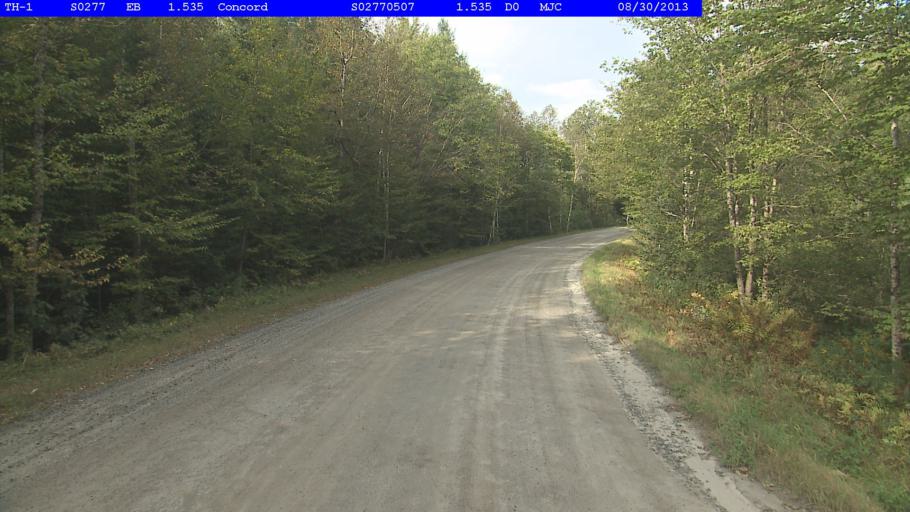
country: US
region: Vermont
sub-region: Caledonia County
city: Lyndonville
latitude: 44.4852
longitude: -71.8658
